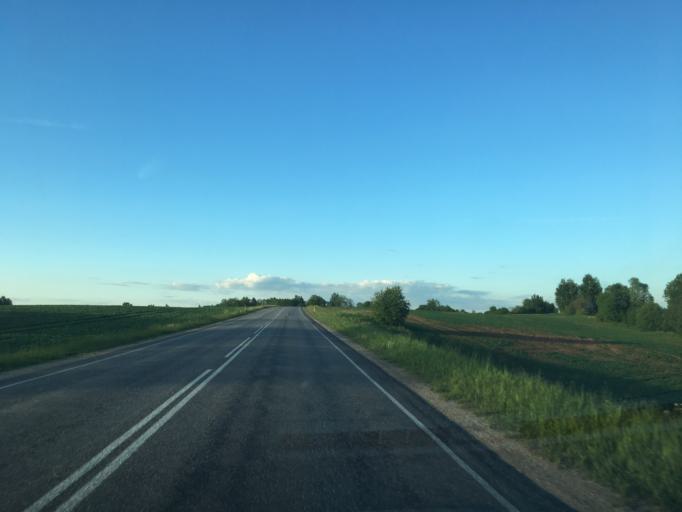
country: EE
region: Tartu
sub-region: Noo vald
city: Noo
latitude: 58.2108
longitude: 26.5897
